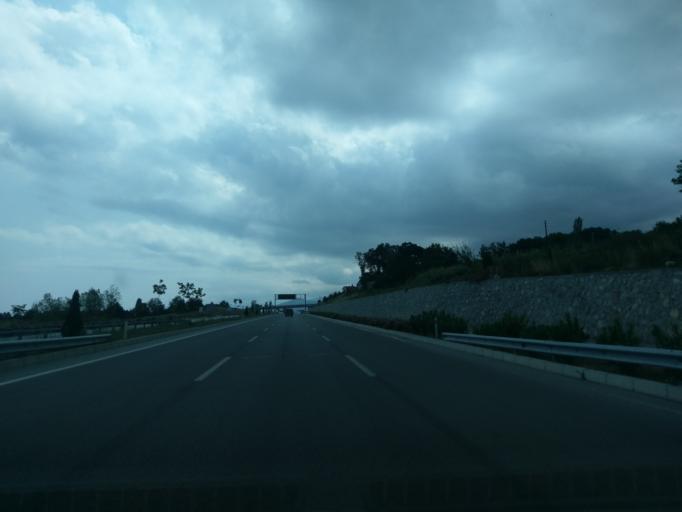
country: TR
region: Sinop
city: Gerze
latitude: 41.7978
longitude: 35.1827
